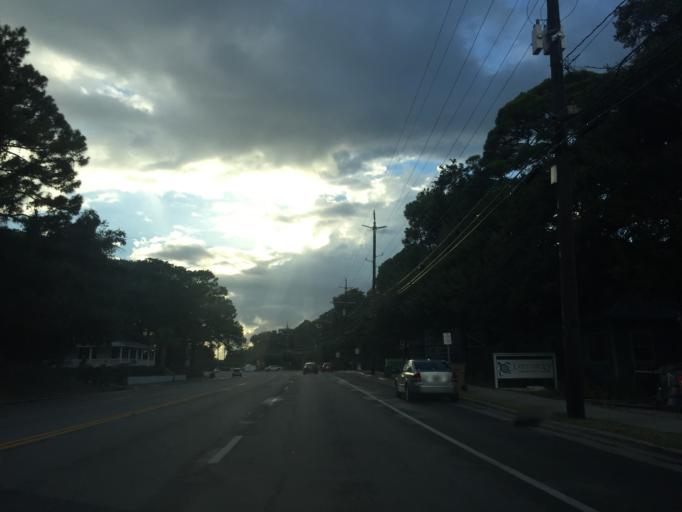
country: US
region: Georgia
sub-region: Chatham County
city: Tybee Island
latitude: 32.0199
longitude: -80.8569
